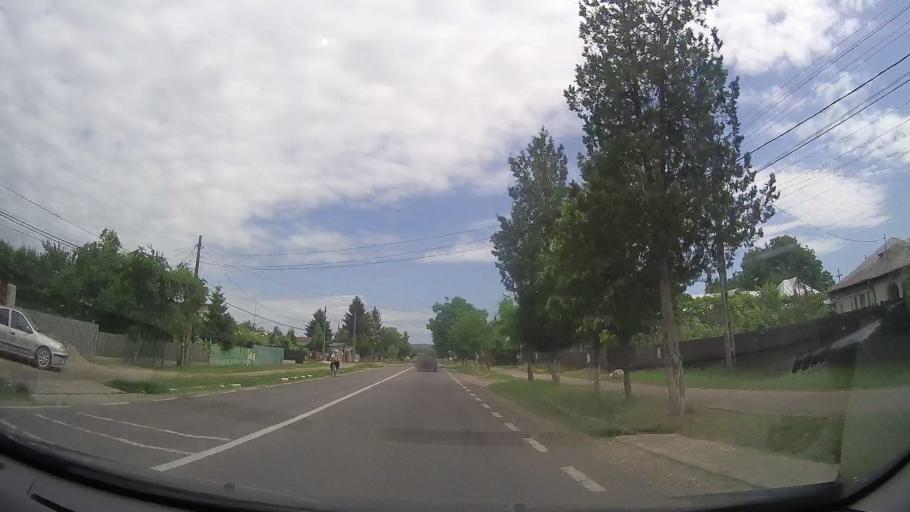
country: RO
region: Prahova
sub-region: Comuna Lipanesti
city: Lipanesti
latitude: 45.0618
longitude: 26.0222
